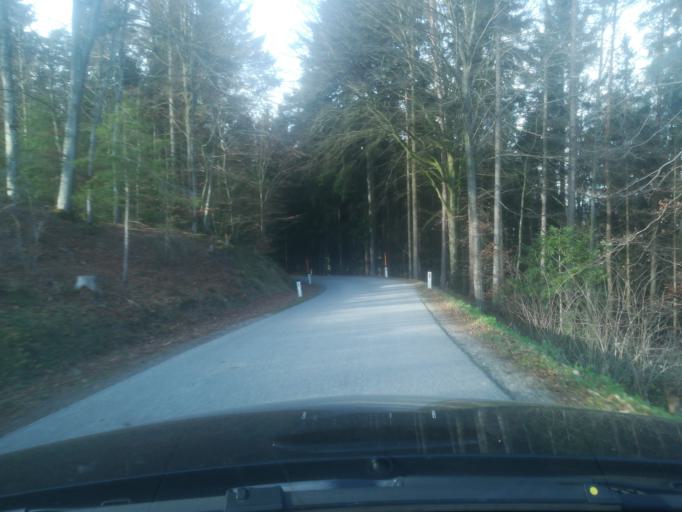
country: AT
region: Upper Austria
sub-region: Politischer Bezirk Perg
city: Perg
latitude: 48.3280
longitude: 14.6521
